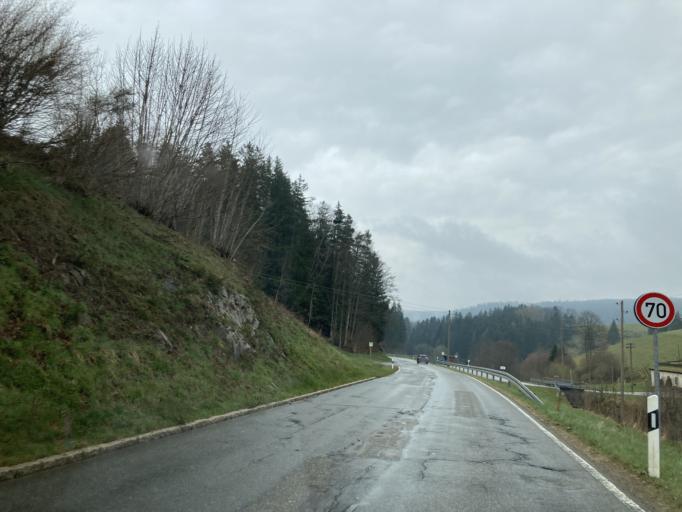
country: DE
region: Baden-Wuerttemberg
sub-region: Freiburg Region
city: Lauterbach/Schwarzwald
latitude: 48.2309
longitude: 8.3080
